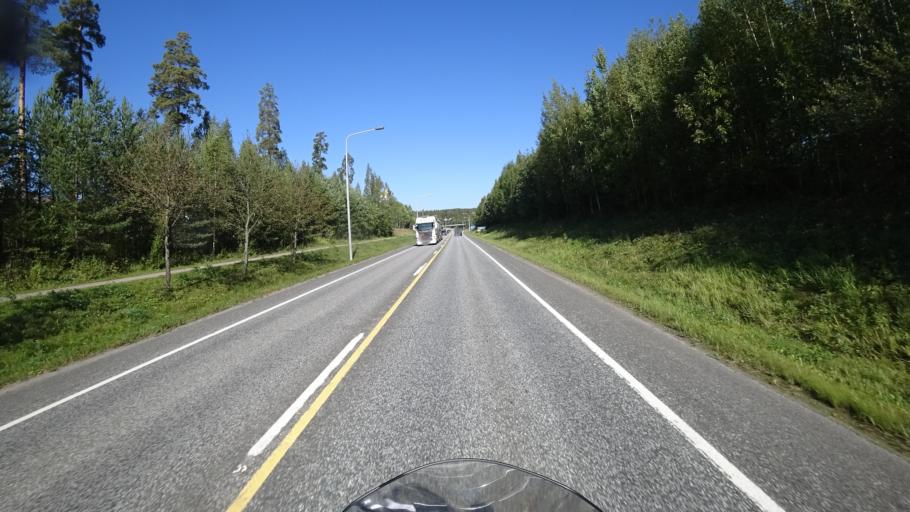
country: FI
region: Uusimaa
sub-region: Helsinki
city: Karkkila
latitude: 60.5287
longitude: 24.2391
